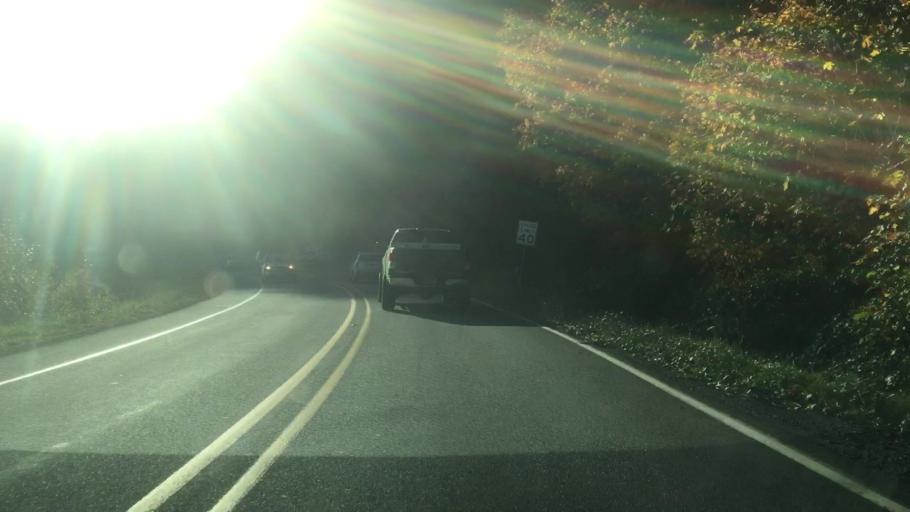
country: US
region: Oregon
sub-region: Clatsop County
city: Astoria
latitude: 46.2493
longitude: -123.8654
